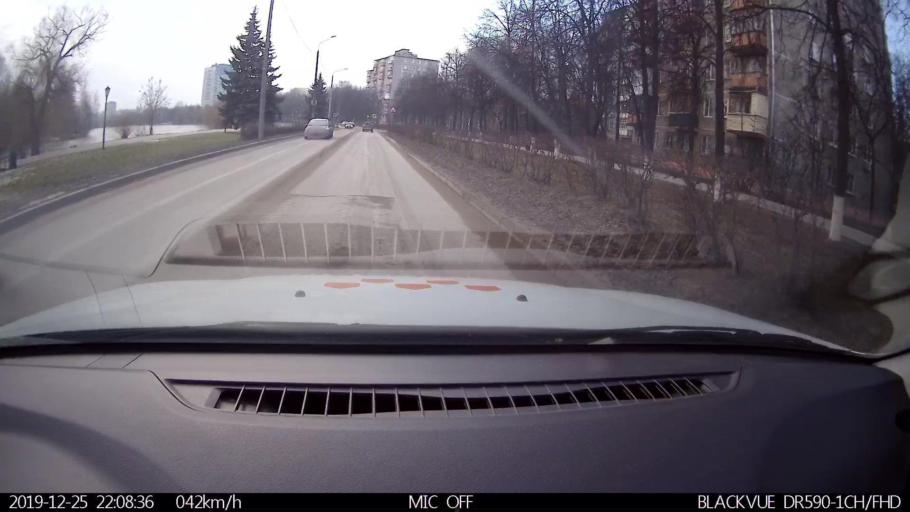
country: RU
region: Nizjnij Novgorod
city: Gorbatovka
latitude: 56.3449
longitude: 43.8508
